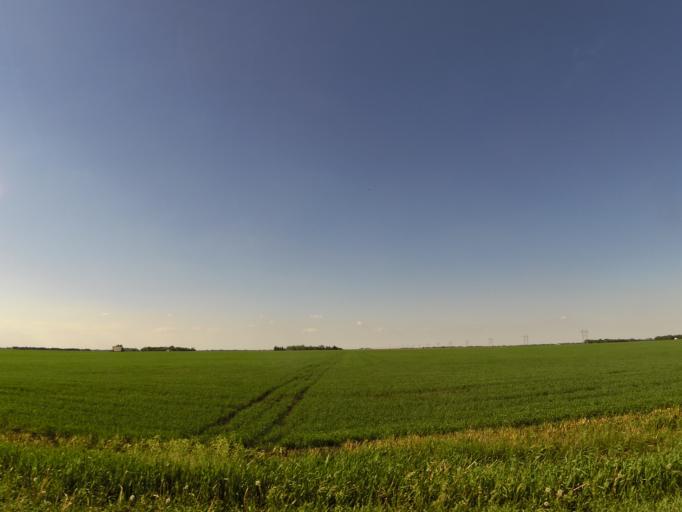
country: US
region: North Dakota
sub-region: Walsh County
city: Grafton
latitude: 48.3687
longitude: -97.2707
